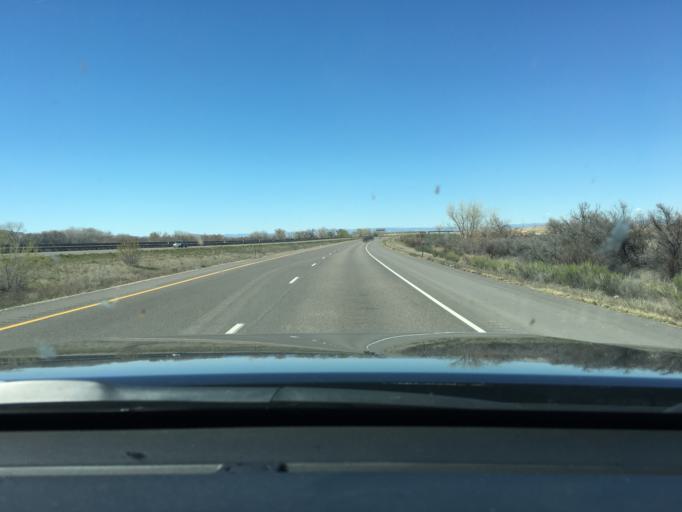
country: US
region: Colorado
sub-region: Mesa County
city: Redlands
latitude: 39.1215
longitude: -108.6768
